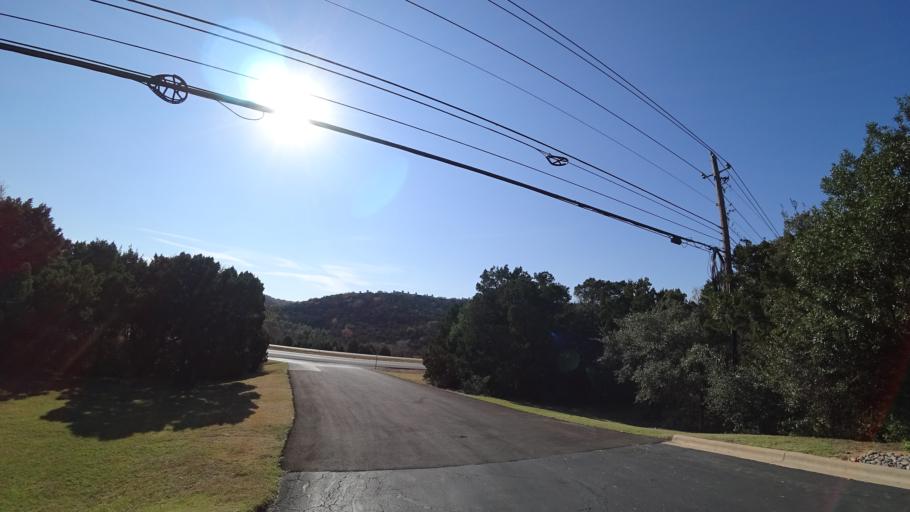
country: US
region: Texas
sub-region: Williamson County
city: Jollyville
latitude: 30.3844
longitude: -97.7694
